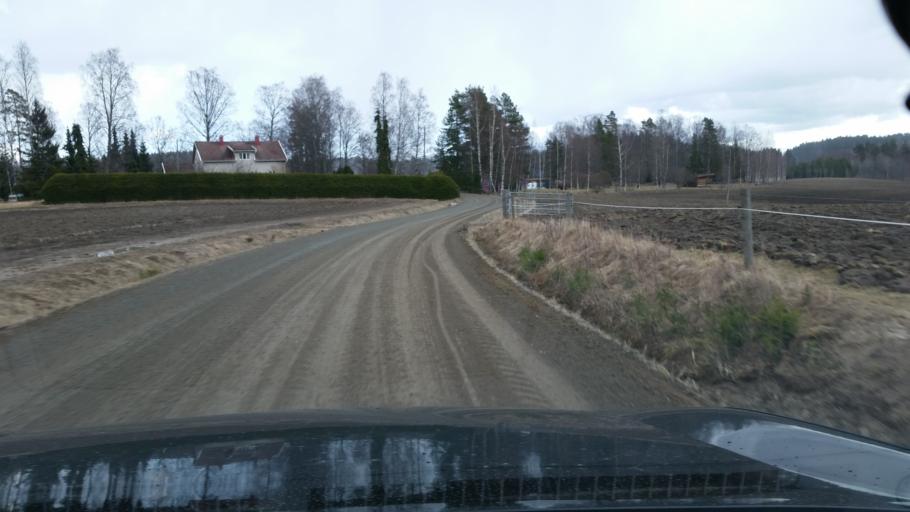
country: FI
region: Uusimaa
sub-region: Helsinki
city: Karjalohja
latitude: 60.1920
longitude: 23.6977
